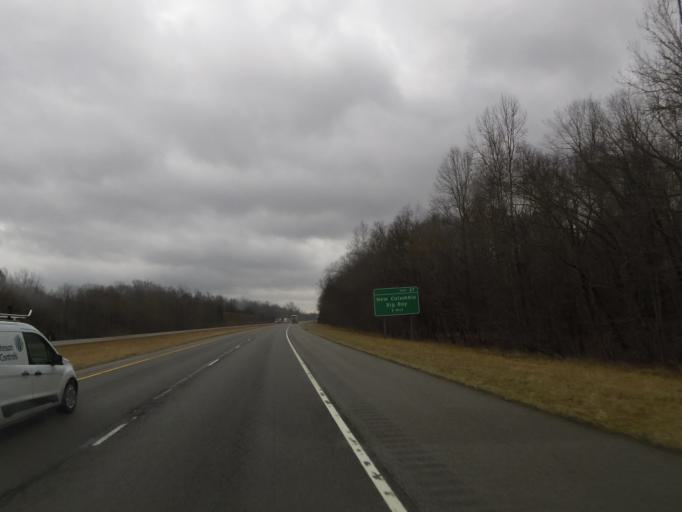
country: US
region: Illinois
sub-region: Johnson County
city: Vienna
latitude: 37.3194
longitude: -88.7607
